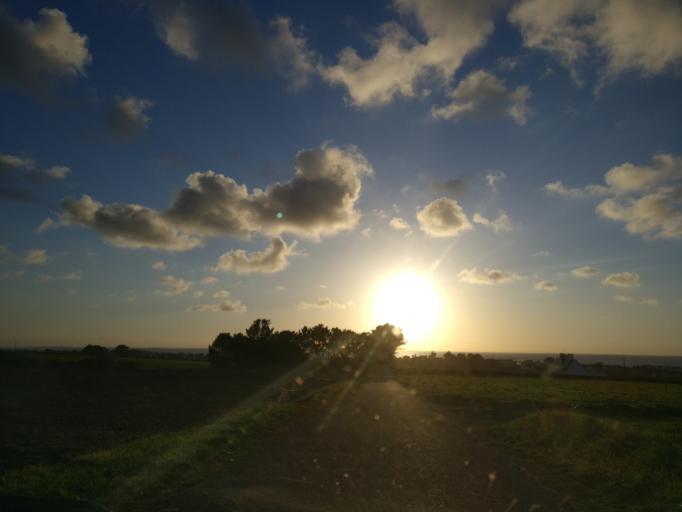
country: FR
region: Brittany
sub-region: Departement du Finistere
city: Lampaul-Plouarzel
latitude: 48.4588
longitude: -4.7510
